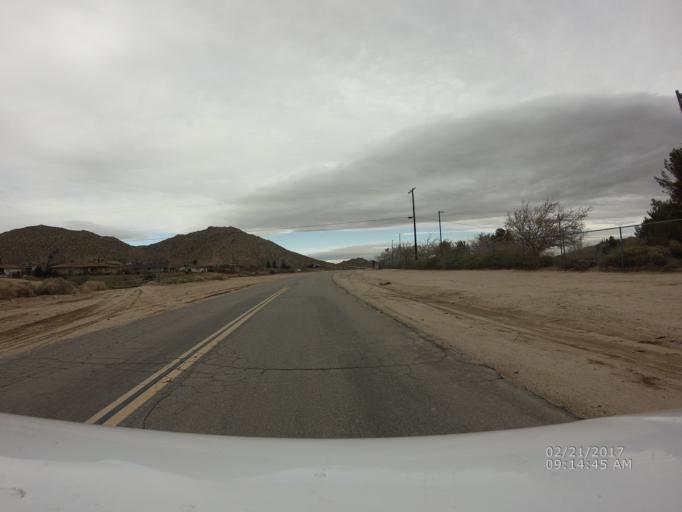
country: US
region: California
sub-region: Los Angeles County
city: Lake Los Angeles
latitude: 34.6032
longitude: -117.8298
